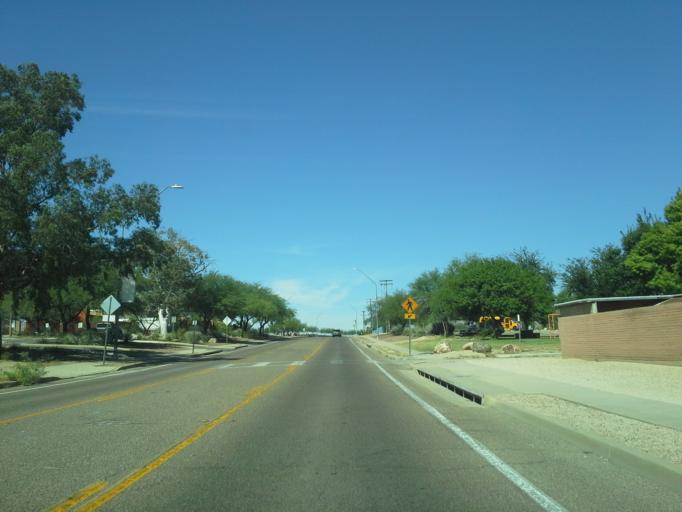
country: US
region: Arizona
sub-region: Pima County
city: South Tucson
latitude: 32.2459
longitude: -110.9688
